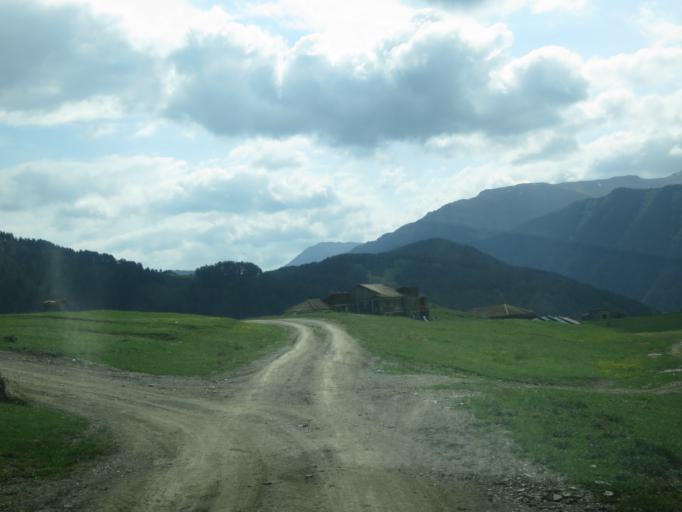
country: RU
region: Chechnya
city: Itum-Kali
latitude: 42.3681
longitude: 45.6347
